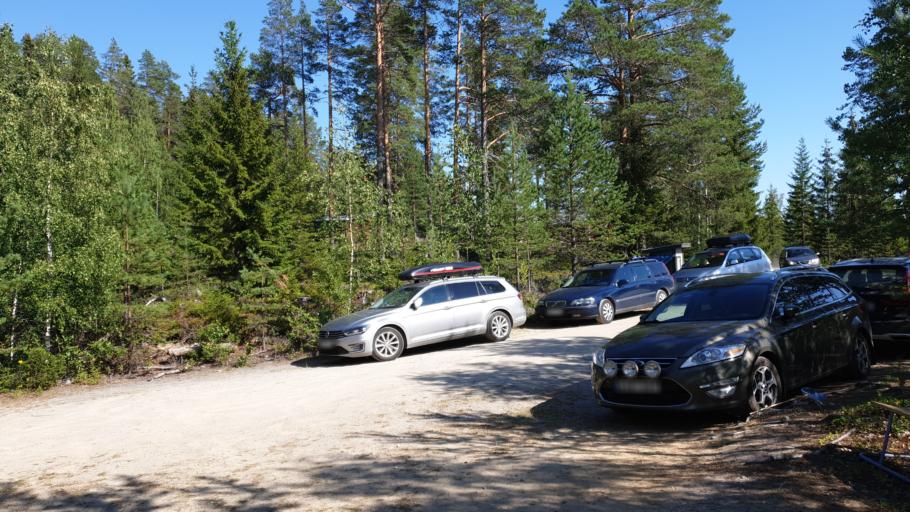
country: SE
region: Vaesternorrland
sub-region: OErnskoeldsviks Kommun
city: Husum
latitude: 63.4959
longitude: 18.9295
